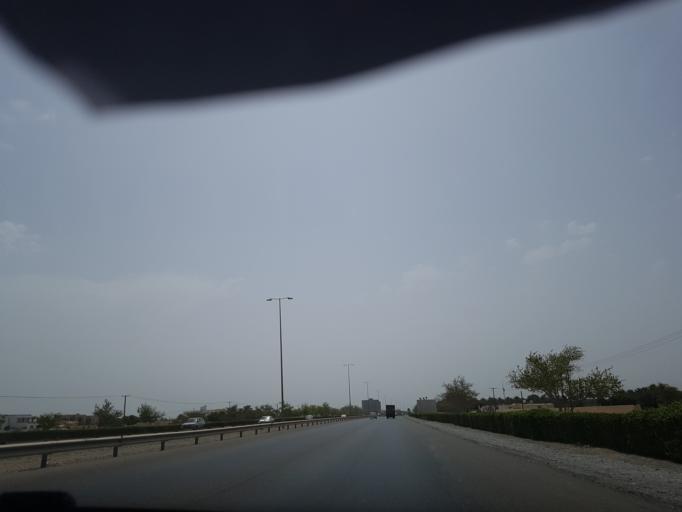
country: OM
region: Al Batinah
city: Barka'
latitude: 23.7169
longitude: 57.7441
